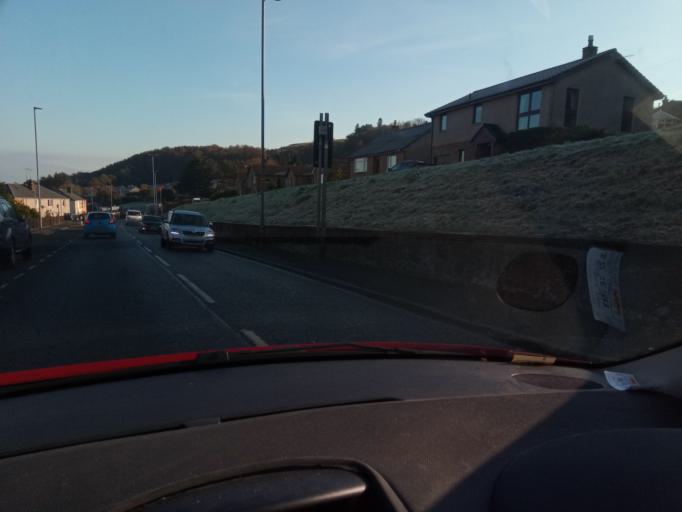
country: GB
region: Scotland
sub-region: The Scottish Borders
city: Hawick
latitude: 55.4289
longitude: -2.7719
